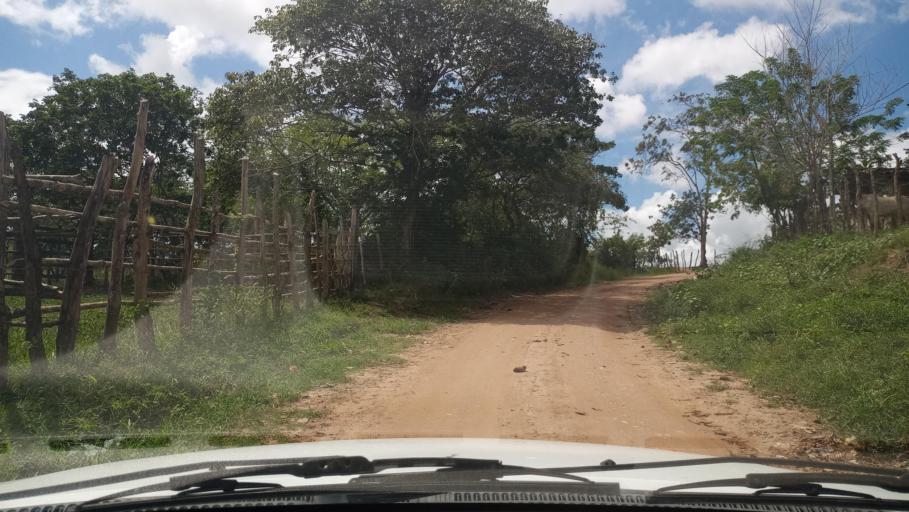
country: BR
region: Rio Grande do Norte
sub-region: Goianinha
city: Goianinha
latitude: -6.2617
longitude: -35.2601
